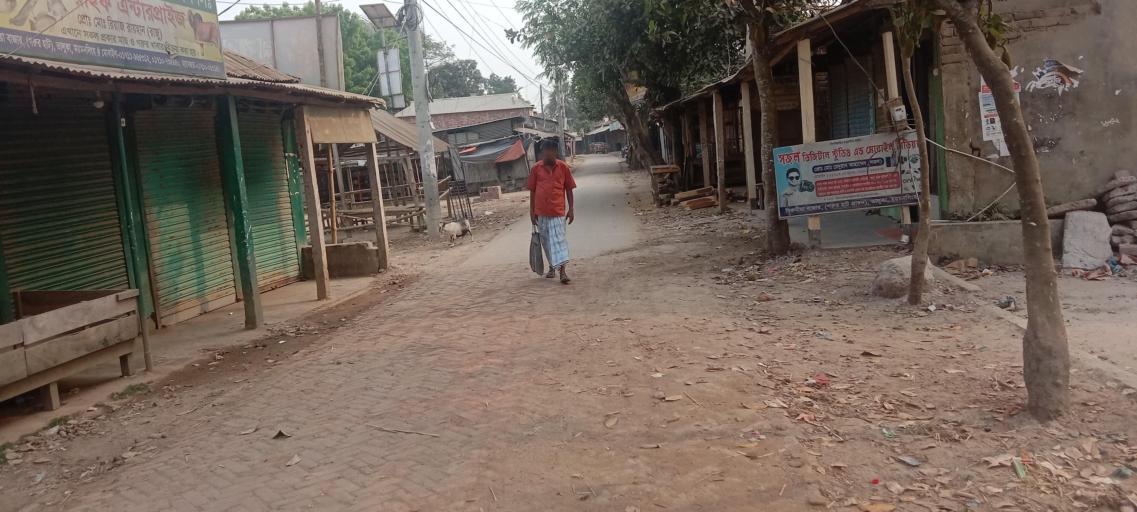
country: BD
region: Dhaka
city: Gafargaon
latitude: 24.3827
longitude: 90.4733
